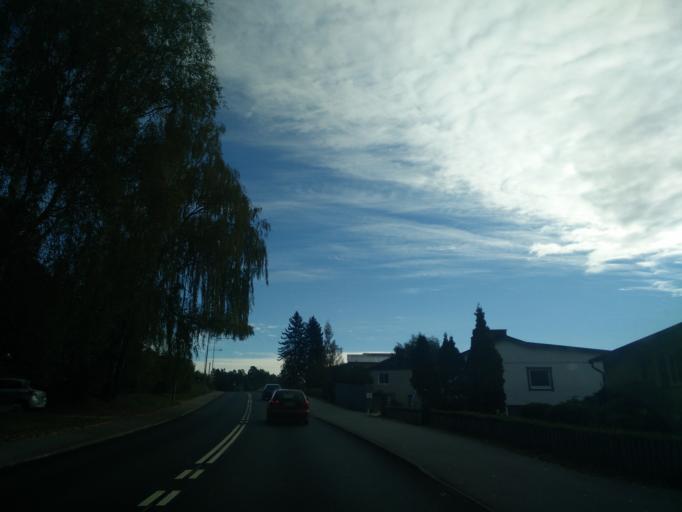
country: SE
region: Stockholm
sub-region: Upplands Vasby Kommun
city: Upplands Vaesby
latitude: 59.5131
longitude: 17.9320
